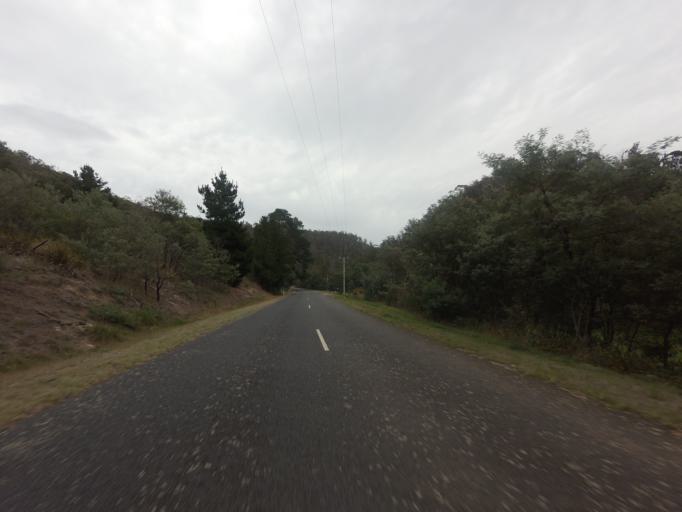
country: AU
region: Tasmania
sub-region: Derwent Valley
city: New Norfolk
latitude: -42.5925
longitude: 147.0318
